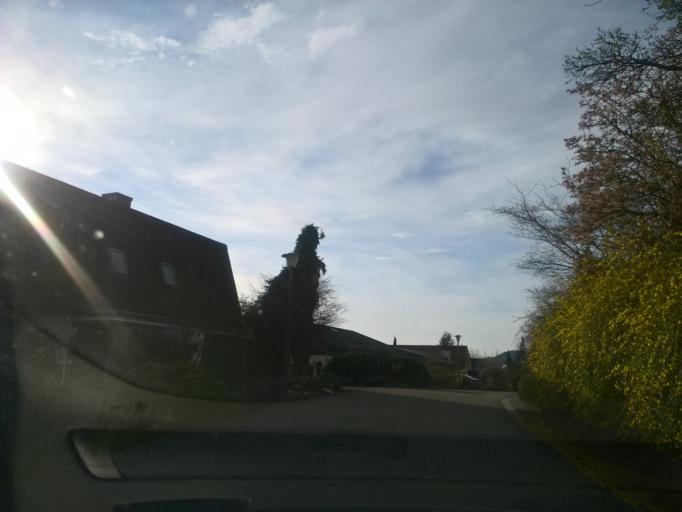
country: CH
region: Zurich
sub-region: Bezirk Buelach
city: Freienstein
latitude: 47.5363
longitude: 8.5836
